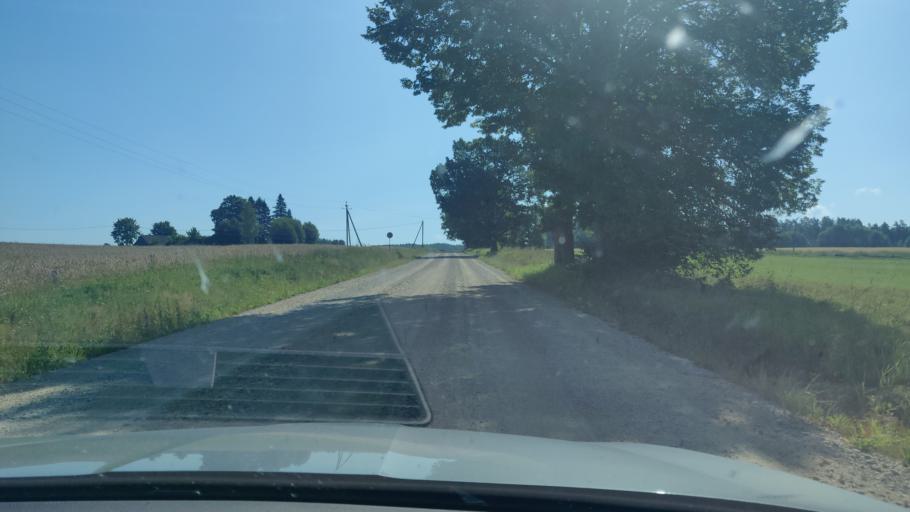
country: EE
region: Tartu
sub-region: Elva linn
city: Elva
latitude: 58.1360
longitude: 26.3938
